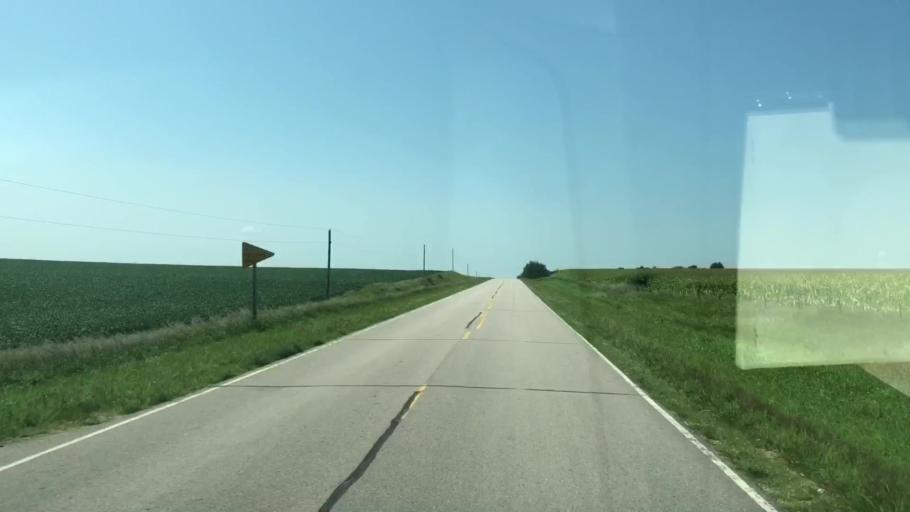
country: US
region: Iowa
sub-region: O'Brien County
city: Sanborn
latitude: 43.2443
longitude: -95.7322
